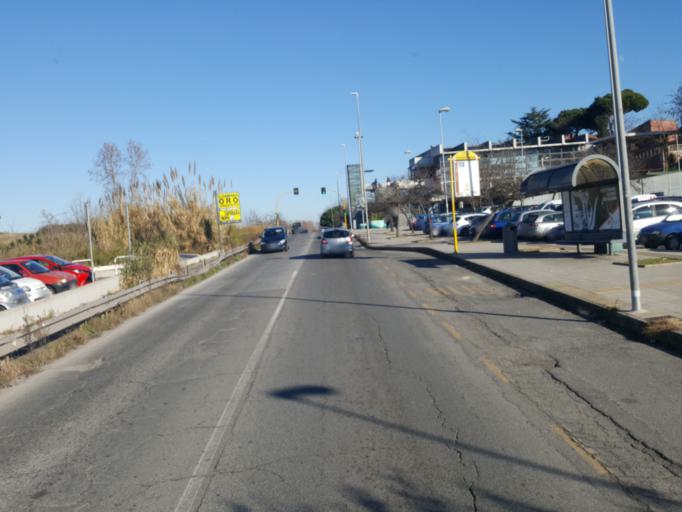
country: IT
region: Latium
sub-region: Citta metropolitana di Roma Capitale
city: Vitinia
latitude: 41.7893
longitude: 12.3763
